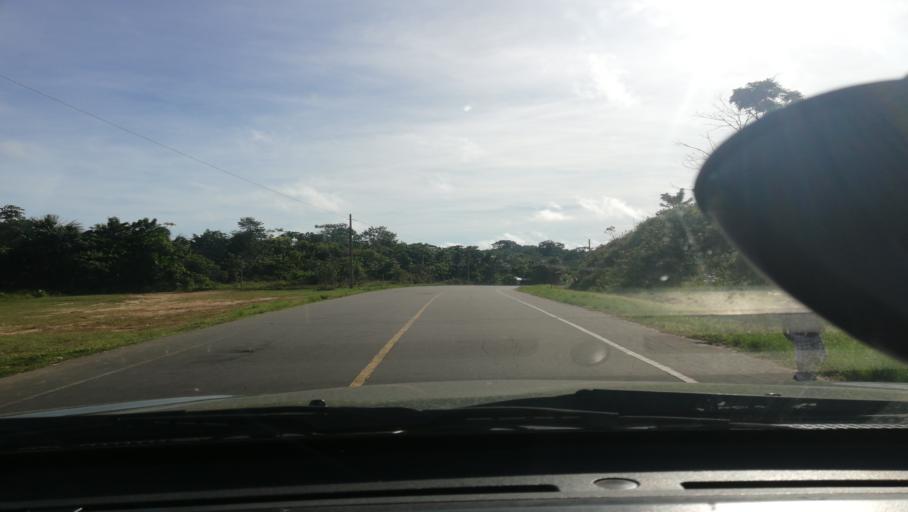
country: PE
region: Loreto
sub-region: Provincia de Loreto
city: Nauta
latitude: -4.3565
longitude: -73.5525
